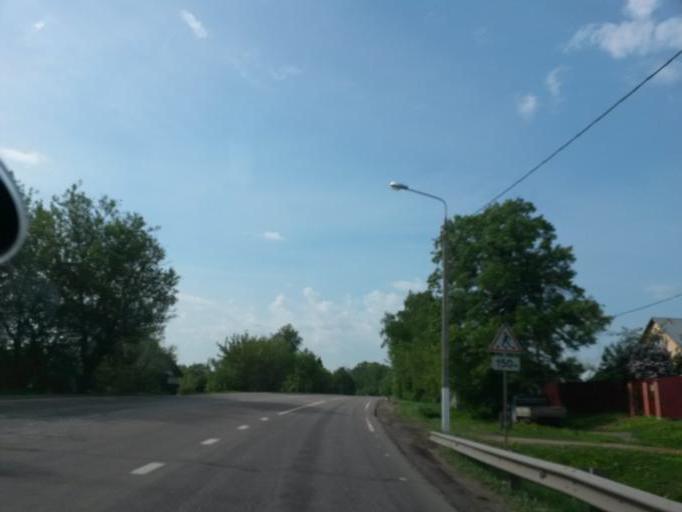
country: RU
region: Moskovskaya
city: Stolbovaya
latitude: 55.2227
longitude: 37.5036
